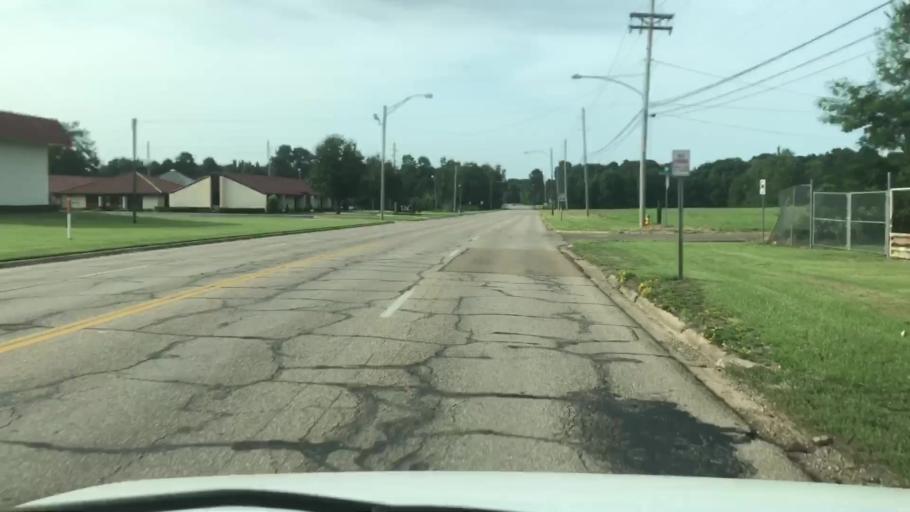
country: US
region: Texas
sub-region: Bowie County
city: Wake Village
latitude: 33.4151
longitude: -94.0804
